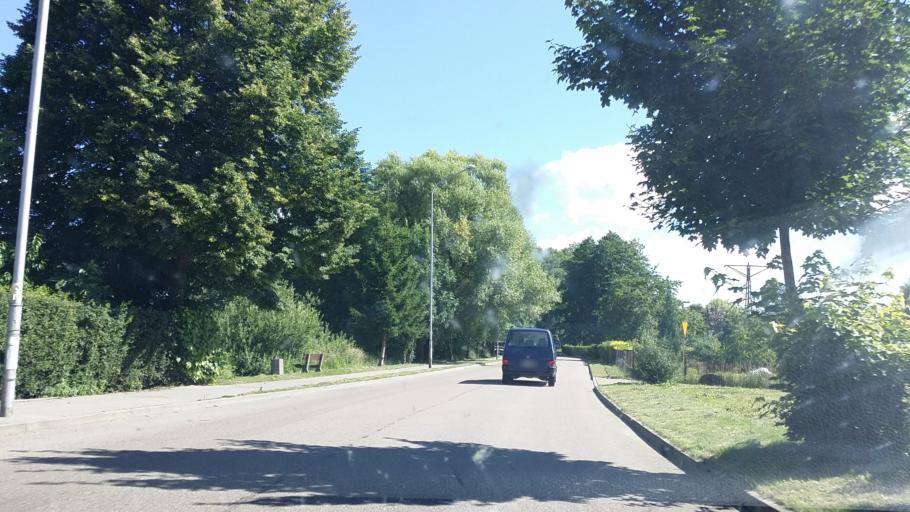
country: PL
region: West Pomeranian Voivodeship
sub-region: Powiat drawski
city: Kalisz Pomorski
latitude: 53.2997
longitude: 15.9068
